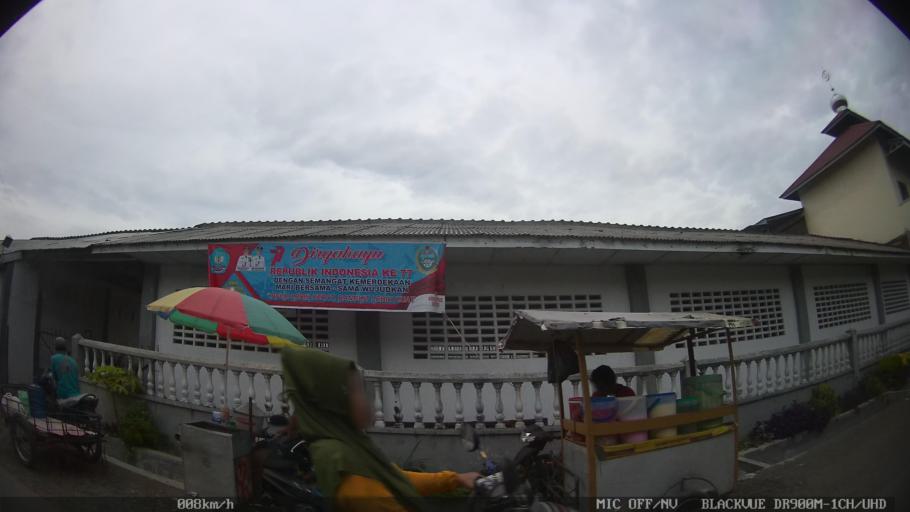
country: ID
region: North Sumatra
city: Sunggal
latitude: 3.6147
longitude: 98.5805
